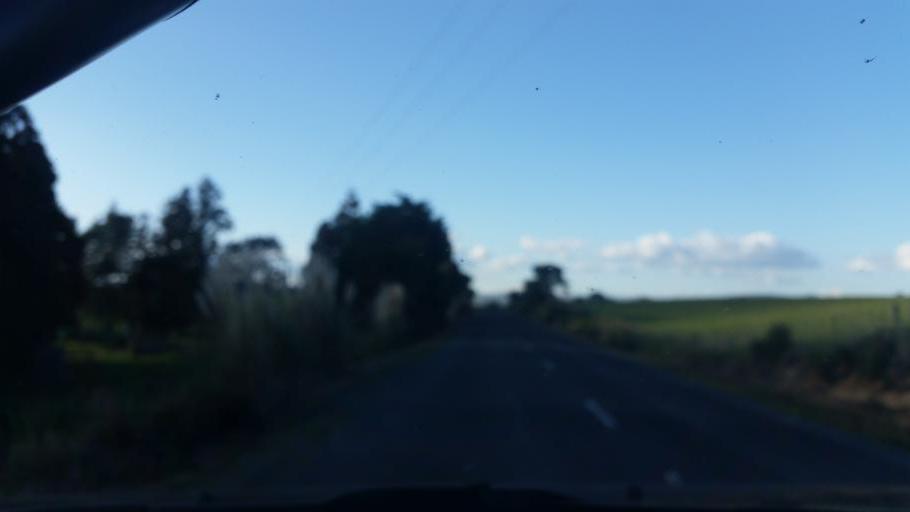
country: NZ
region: Northland
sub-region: Kaipara District
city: Dargaville
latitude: -36.2024
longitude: 174.0461
